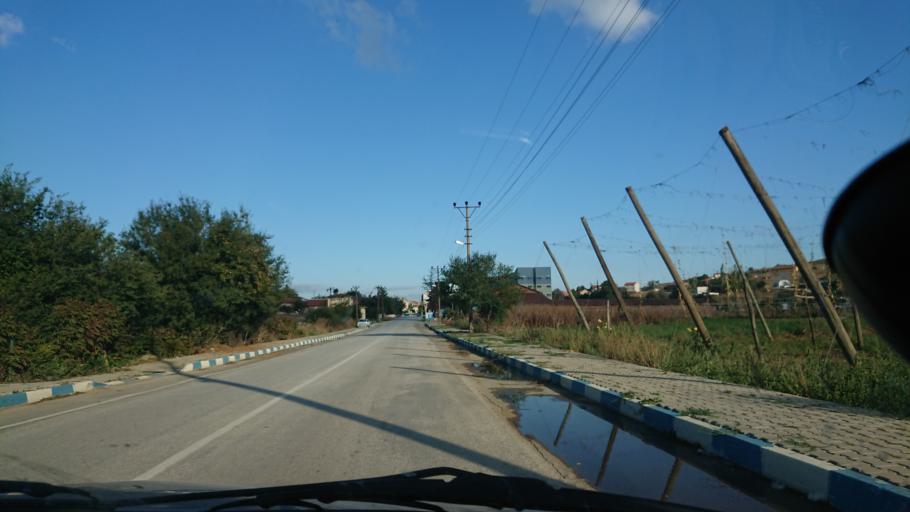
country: TR
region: Bilecik
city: Pazaryeri
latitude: 39.9991
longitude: 29.8906
